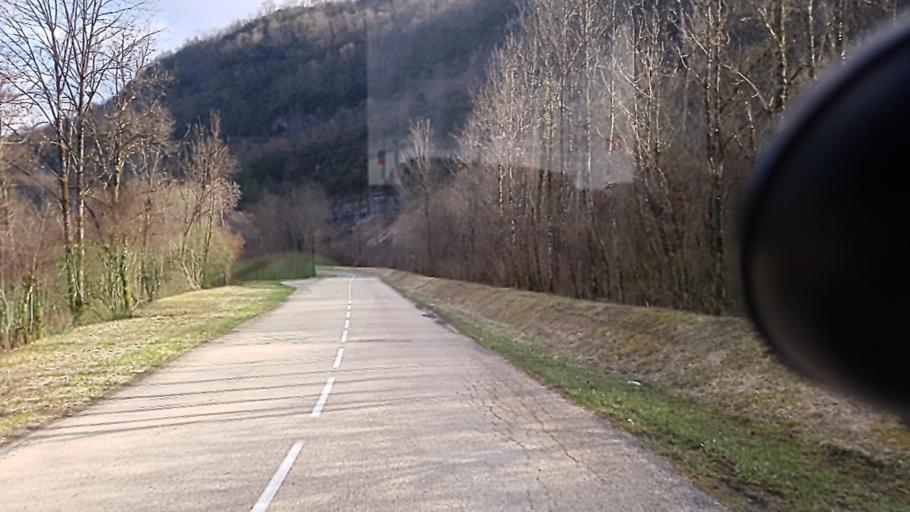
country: FR
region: Rhone-Alpes
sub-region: Departement de l'Ain
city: Dortan
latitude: 46.3246
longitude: 5.6438
